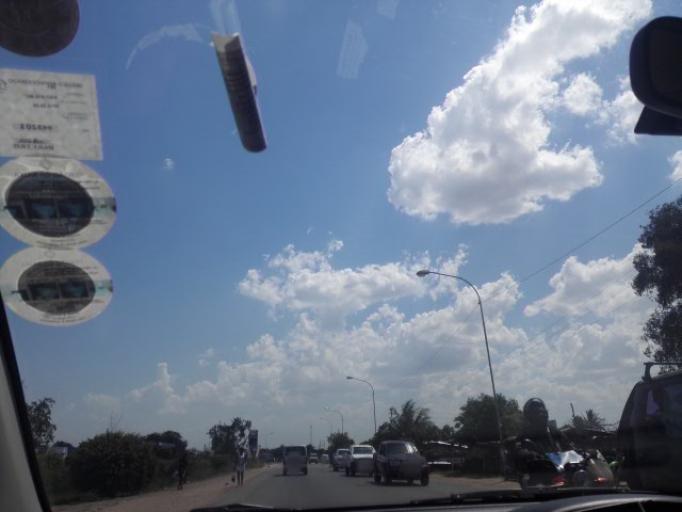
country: MZ
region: Maputo
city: Matola
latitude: -25.9703
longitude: 32.4415
